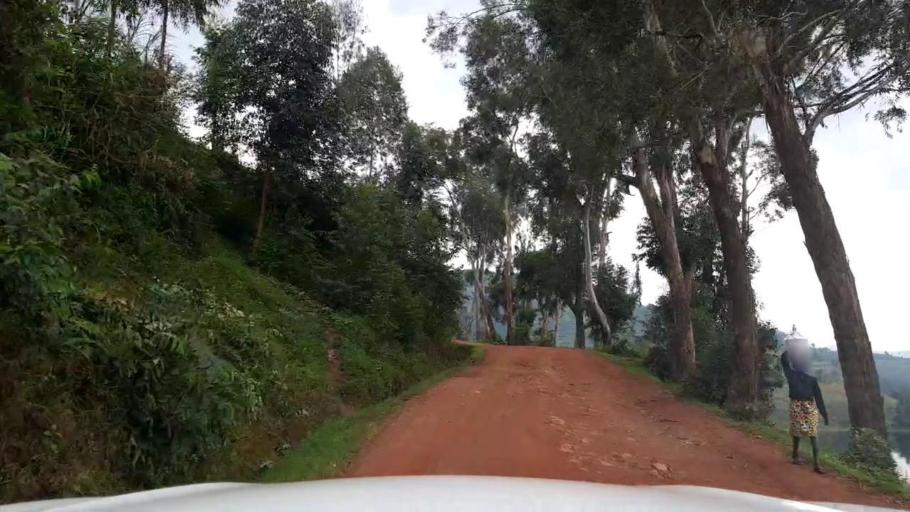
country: UG
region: Western Region
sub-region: Kisoro District
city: Kisoro
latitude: -1.3882
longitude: 29.7976
